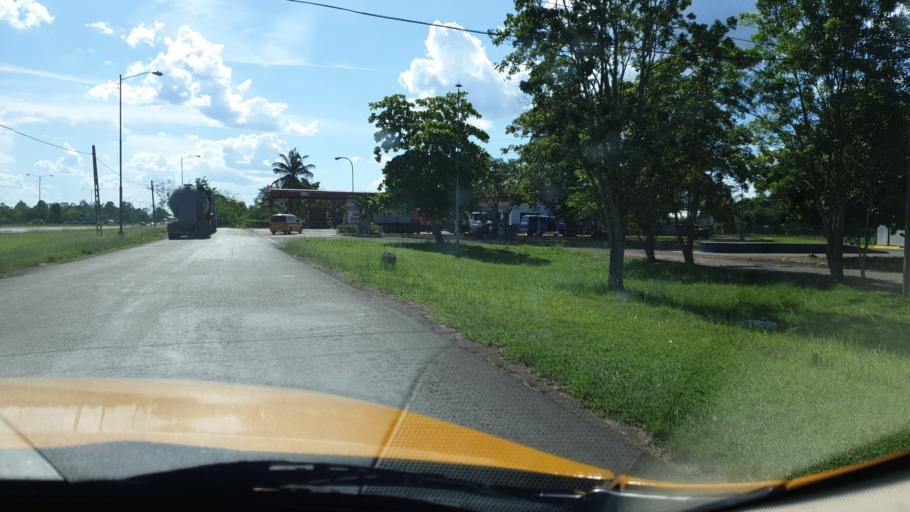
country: CU
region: Cienfuegos
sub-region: Municipio de Aguada de Pasajeros
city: Aguada de Pasajeros
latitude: 22.4046
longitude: -80.8656
